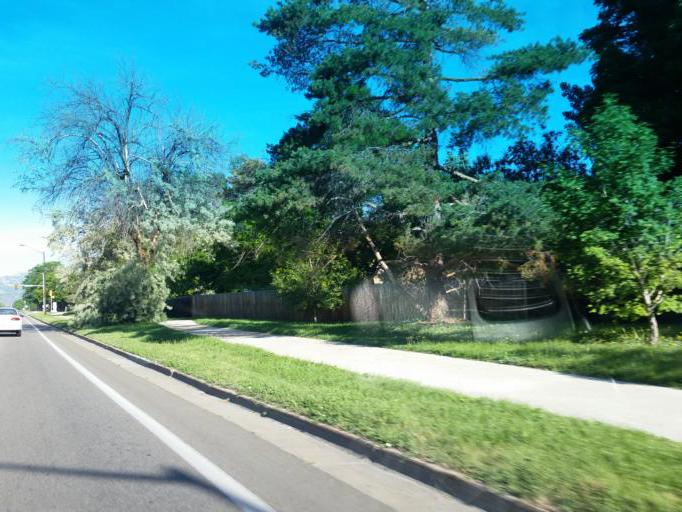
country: US
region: Colorado
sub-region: Larimer County
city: Fort Collins
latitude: 40.5381
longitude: -105.0639
